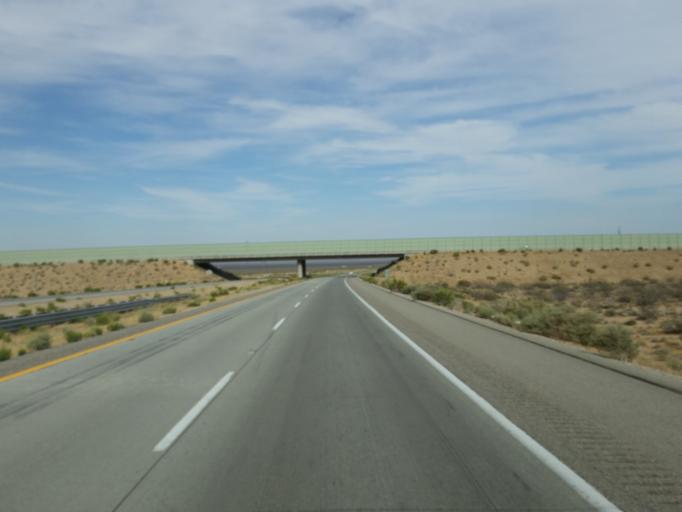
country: US
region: California
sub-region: Kern County
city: Mojave
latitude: 35.1141
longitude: -118.1816
